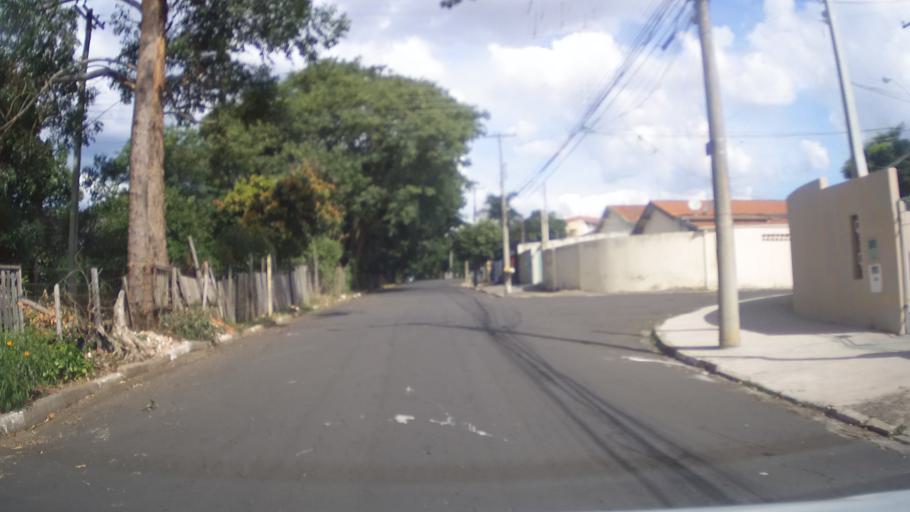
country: BR
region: Sao Paulo
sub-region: Campinas
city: Campinas
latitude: -22.8825
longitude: -47.1103
